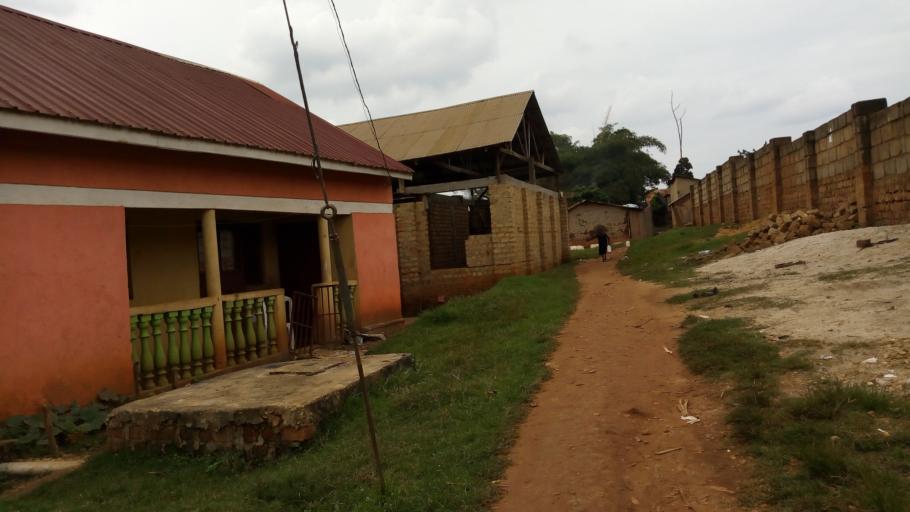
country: UG
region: Central Region
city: Kampala Central Division
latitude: 0.3589
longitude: 32.5608
